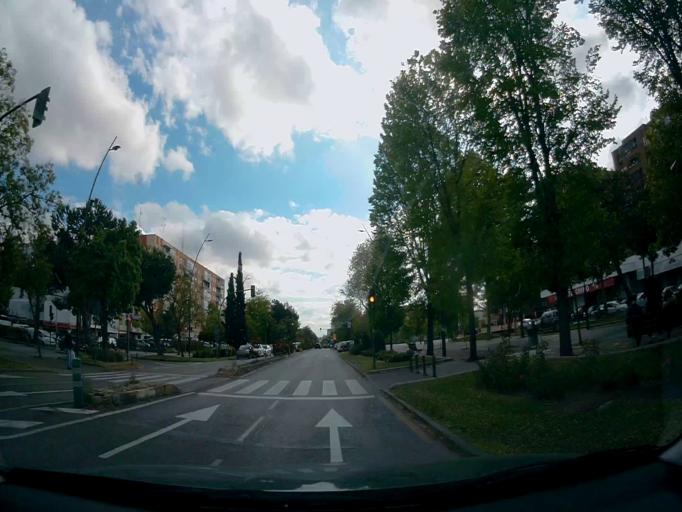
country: ES
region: Madrid
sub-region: Provincia de Madrid
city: Mostoles
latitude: 40.3304
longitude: -3.8564
